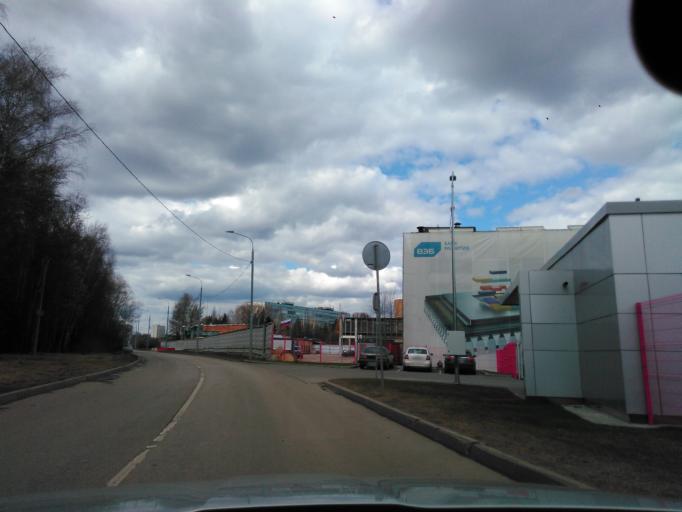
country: RU
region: Moscow
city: Zelenograd
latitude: 55.9795
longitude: 37.2135
